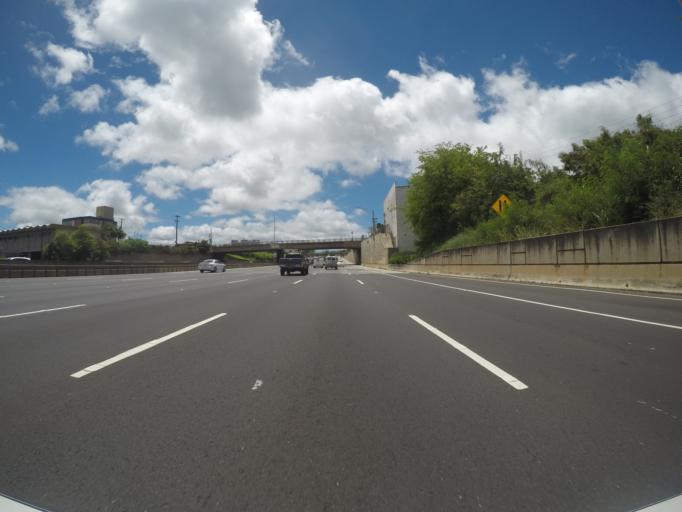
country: US
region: Hawaii
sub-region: Honolulu County
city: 'Aiea
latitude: 21.3792
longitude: -157.9284
